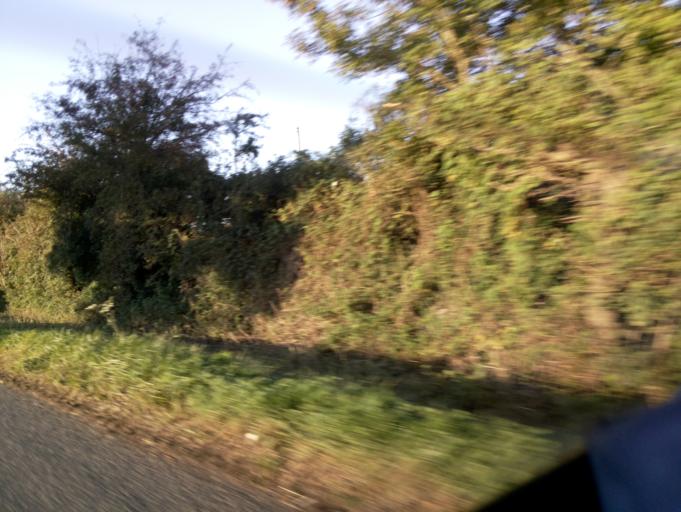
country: GB
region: England
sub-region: Worcestershire
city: Upton upon Severn
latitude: 52.0012
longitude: -2.2350
